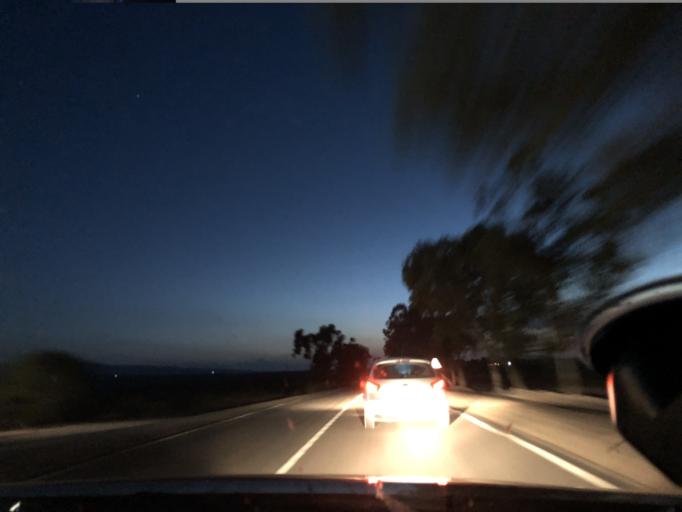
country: TN
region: Al Qasrayn
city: Kasserine
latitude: 35.2402
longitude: 8.9877
